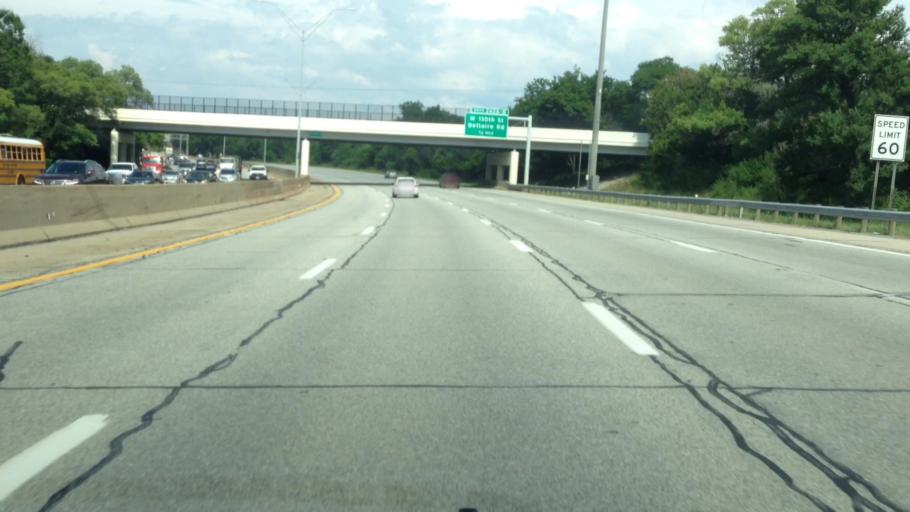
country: US
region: Ohio
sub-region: Cuyahoga County
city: Brook Park
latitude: 41.4387
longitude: -81.7920
